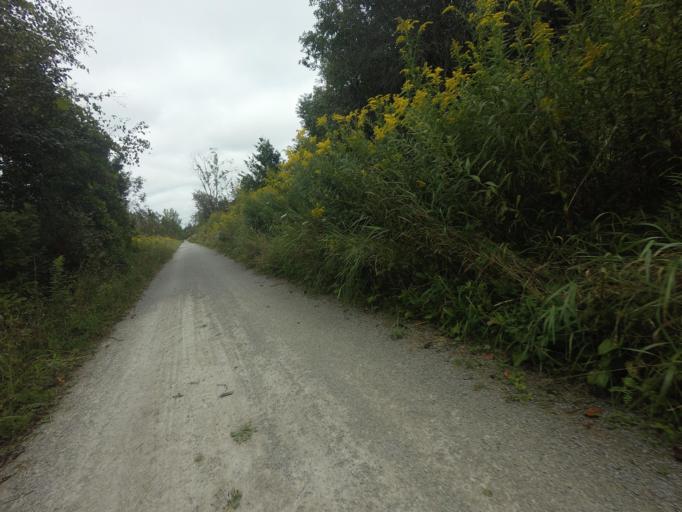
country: CA
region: Ontario
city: Uxbridge
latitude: 44.2465
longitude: -79.0394
